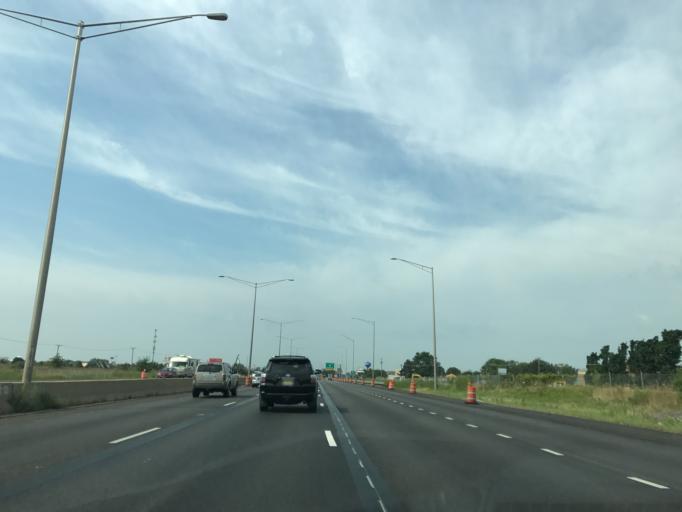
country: US
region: Illinois
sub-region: Will County
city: Bolingbrook
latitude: 41.6899
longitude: -88.0590
